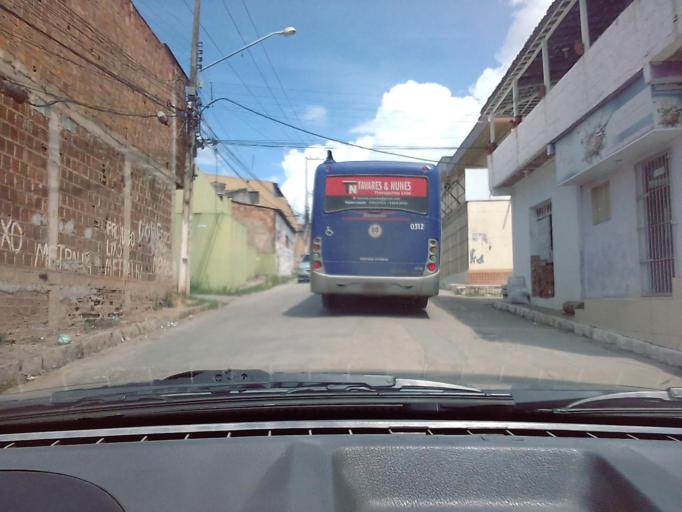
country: BR
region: Pernambuco
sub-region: Vitoria De Santo Antao
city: Vitoria de Santo Antao
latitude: -8.1276
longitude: -35.2915
